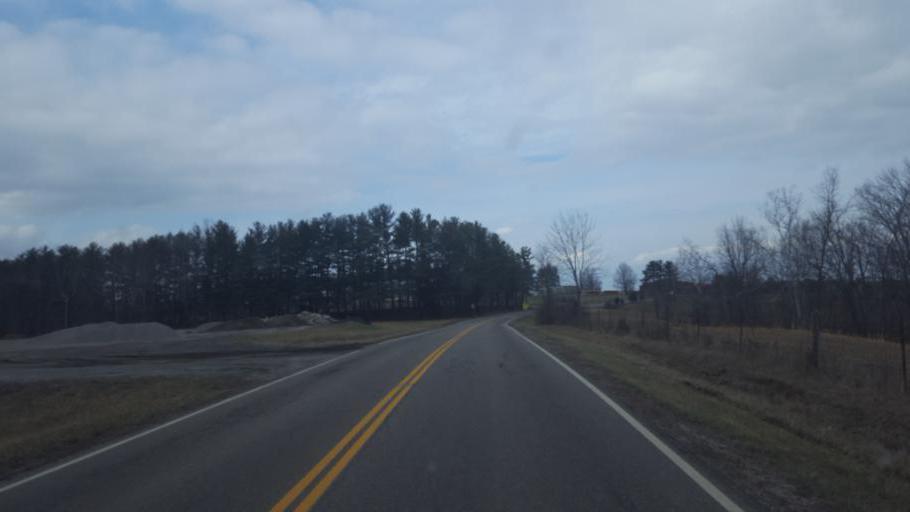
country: US
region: Ohio
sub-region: Jackson County
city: Oak Hill
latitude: 38.8193
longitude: -82.4012
